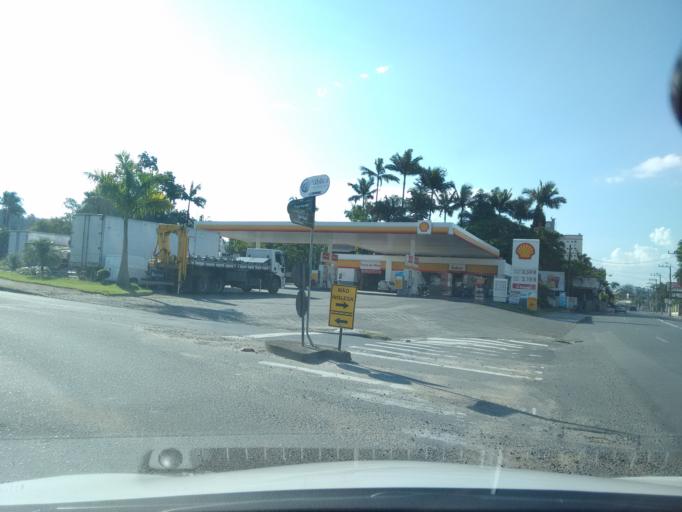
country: BR
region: Santa Catarina
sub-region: Blumenau
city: Blumenau
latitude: -26.8973
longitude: -49.0789
